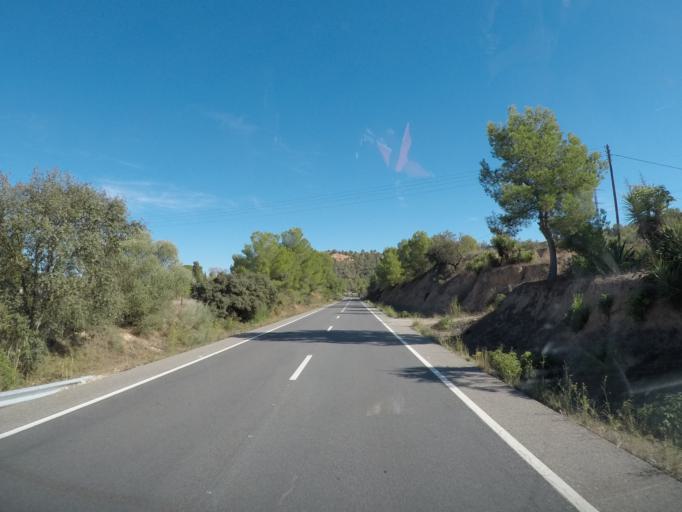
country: ES
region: Catalonia
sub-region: Provincia de Tarragona
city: Ginestar
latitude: 41.0533
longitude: 0.6610
